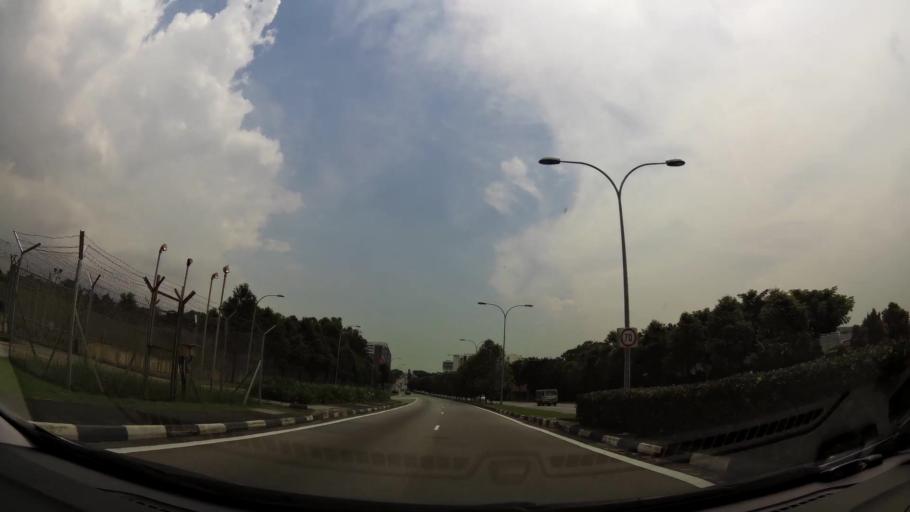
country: SG
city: Singapore
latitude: 1.3391
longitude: 103.9006
